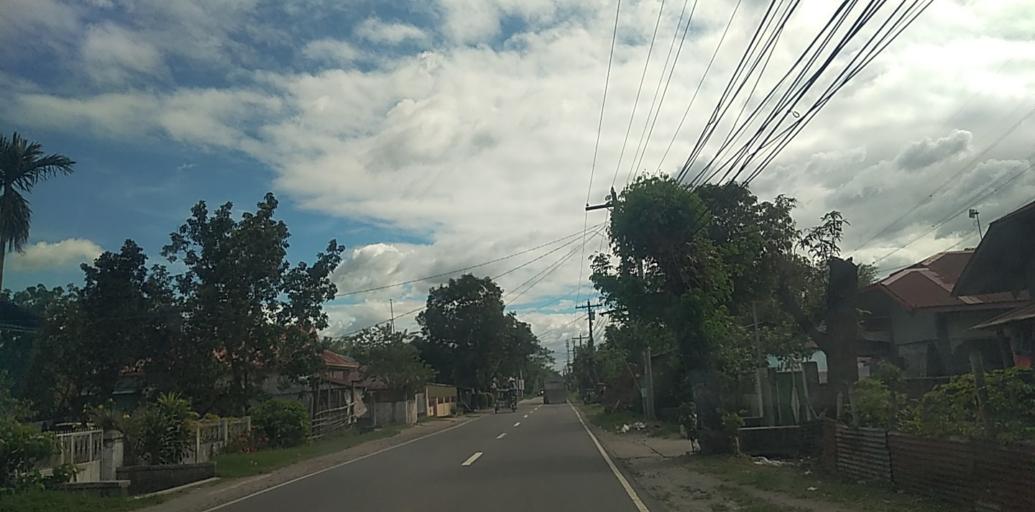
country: PH
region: Central Luzon
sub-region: Province of Pampanga
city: Buensuseso
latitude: 15.1849
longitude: 120.6757
